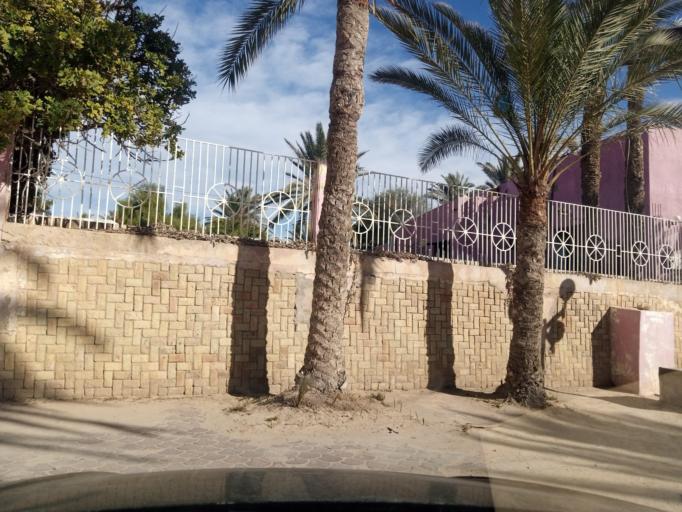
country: TN
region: Qabis
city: Gabes
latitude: 33.8899
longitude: 10.1155
